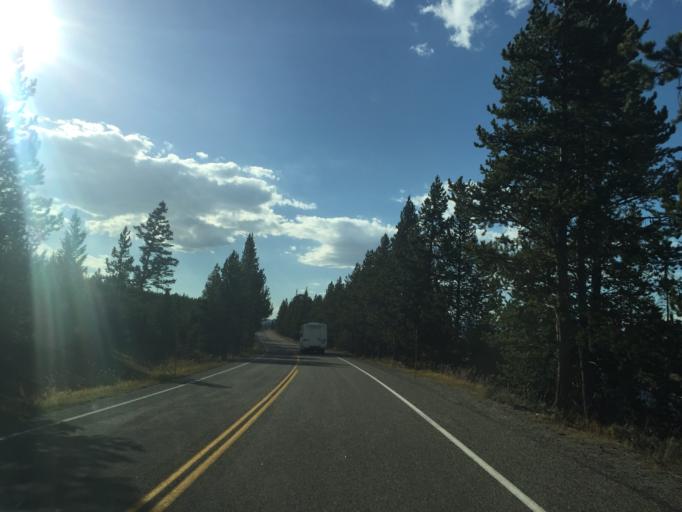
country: US
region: Montana
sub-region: Gallatin County
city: West Yellowstone
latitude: 44.6501
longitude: -111.0086
